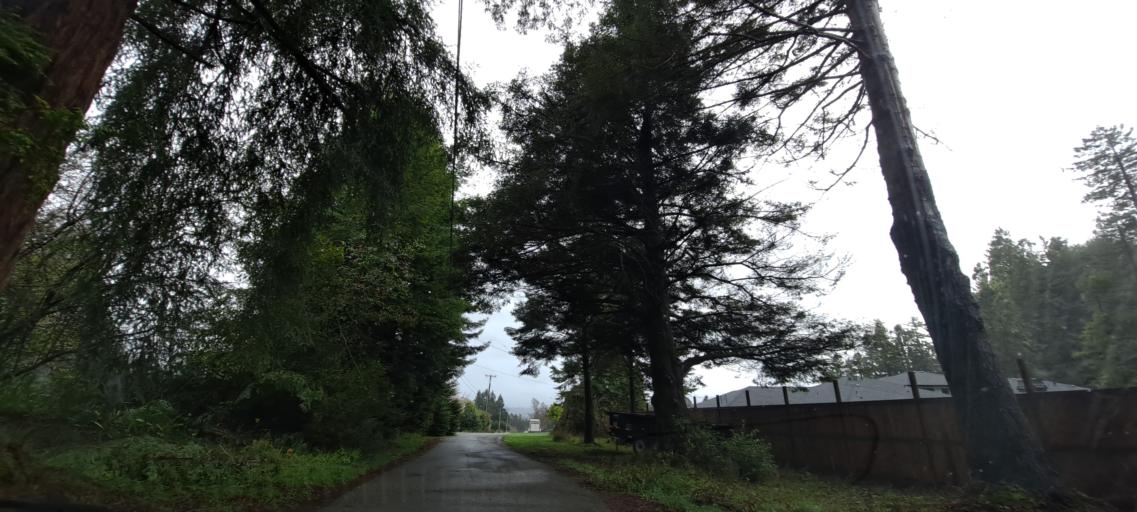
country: US
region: California
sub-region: Humboldt County
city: Fortuna
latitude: 40.6064
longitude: -124.1364
